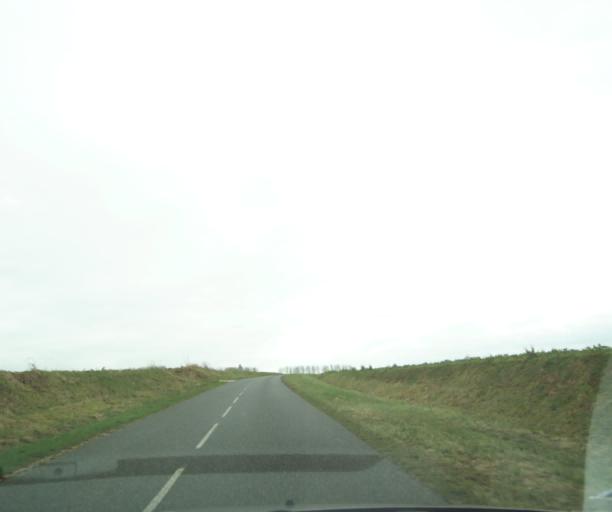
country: FR
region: Picardie
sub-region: Departement de l'Oise
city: Noyon
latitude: 49.5948
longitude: 2.9921
